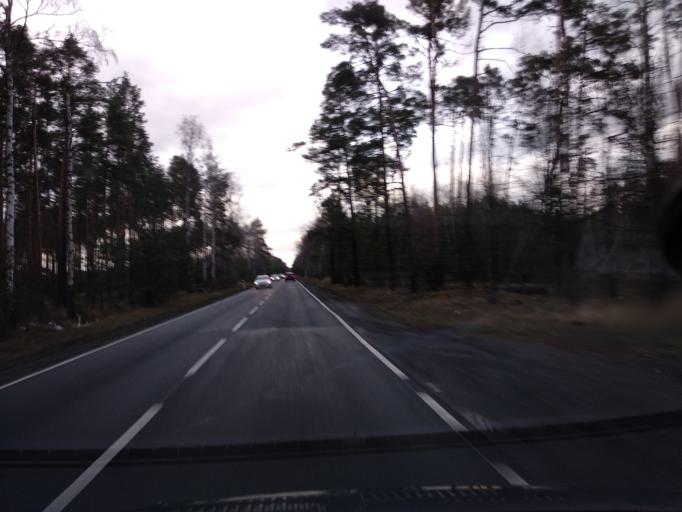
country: PL
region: Lower Silesian Voivodeship
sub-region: Powiat olesnicki
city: Miedzyborz
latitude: 51.4492
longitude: 17.7165
